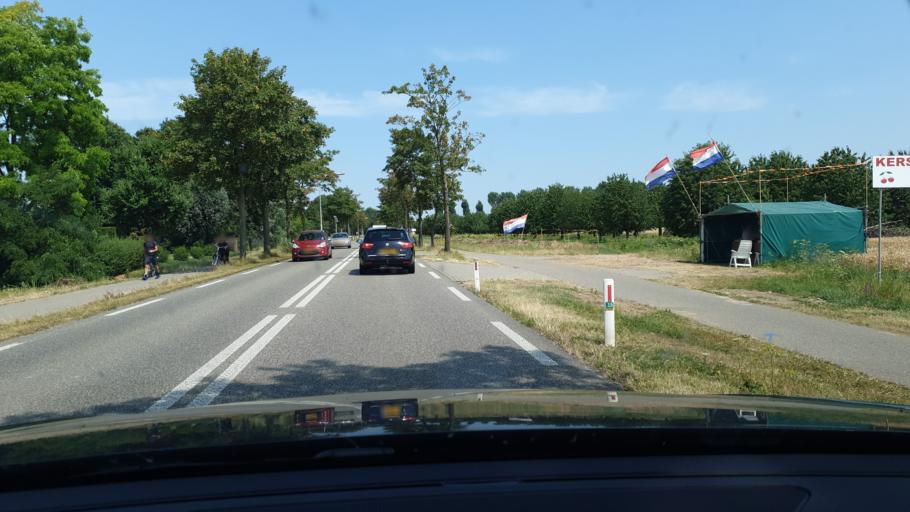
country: NL
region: Gelderland
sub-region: Gemeente Overbetuwe
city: Elst
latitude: 51.9070
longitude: 5.9115
